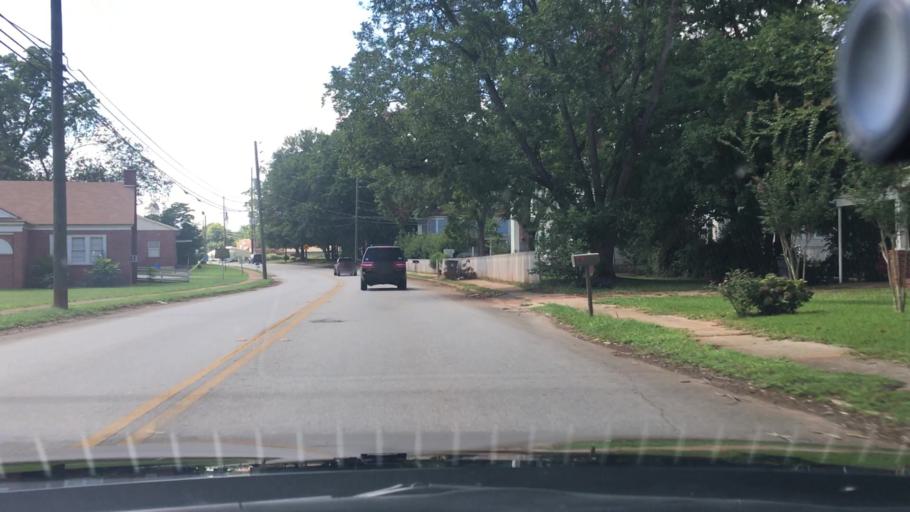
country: US
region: Georgia
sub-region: Jasper County
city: Monticello
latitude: 33.3026
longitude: -83.6793
